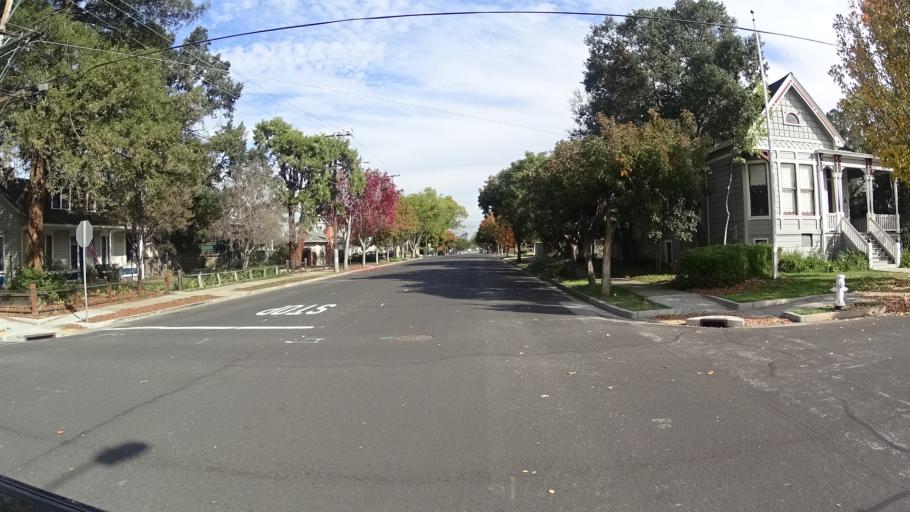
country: US
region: California
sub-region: Santa Clara County
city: Santa Clara
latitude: 37.3512
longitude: -121.9468
